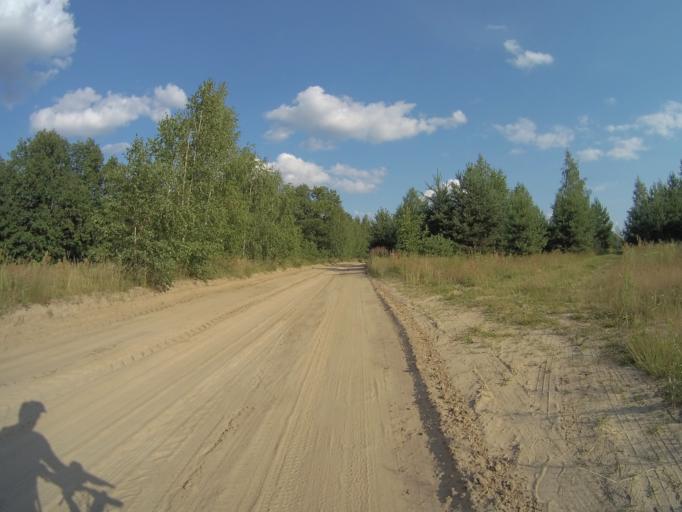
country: RU
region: Vladimir
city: Orgtrud
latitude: 56.1491
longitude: 40.6136
